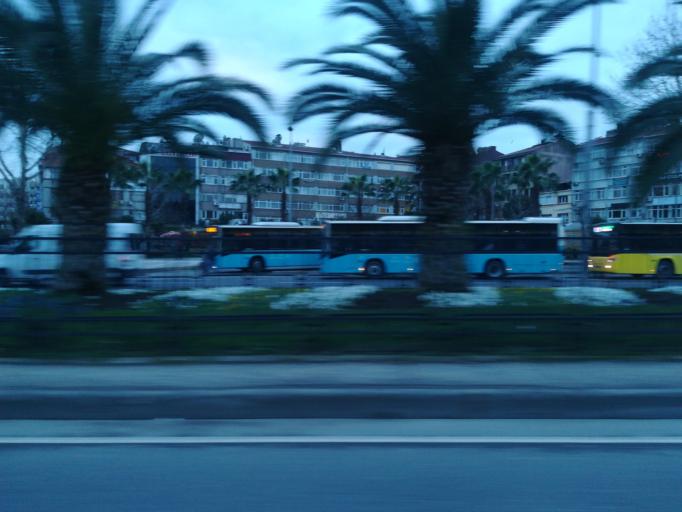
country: TR
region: Istanbul
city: Istanbul
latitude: 41.0114
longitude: 28.9486
